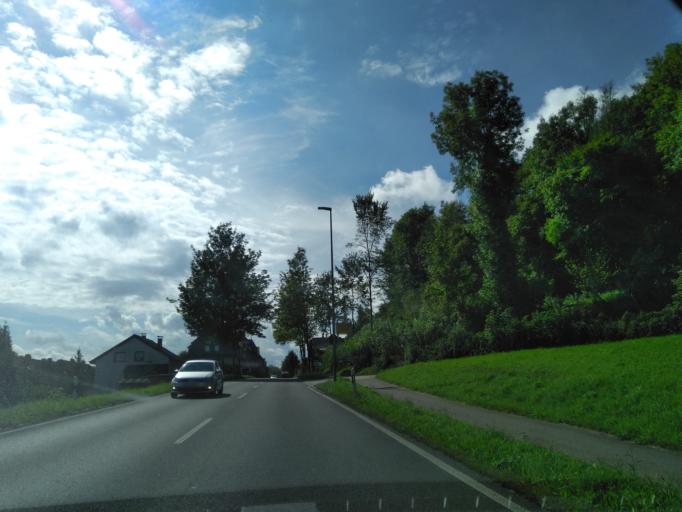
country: DE
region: Baden-Wuerttemberg
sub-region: Regierungsbezirk Stuttgart
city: Besigheim
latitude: 48.9744
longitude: 9.1436
